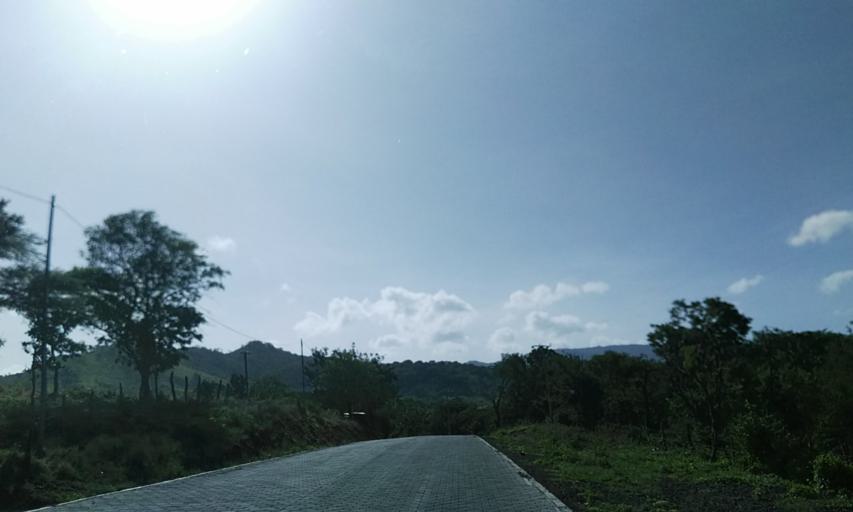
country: NI
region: Matagalpa
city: Ciudad Dario
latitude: 12.7325
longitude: -86.0584
